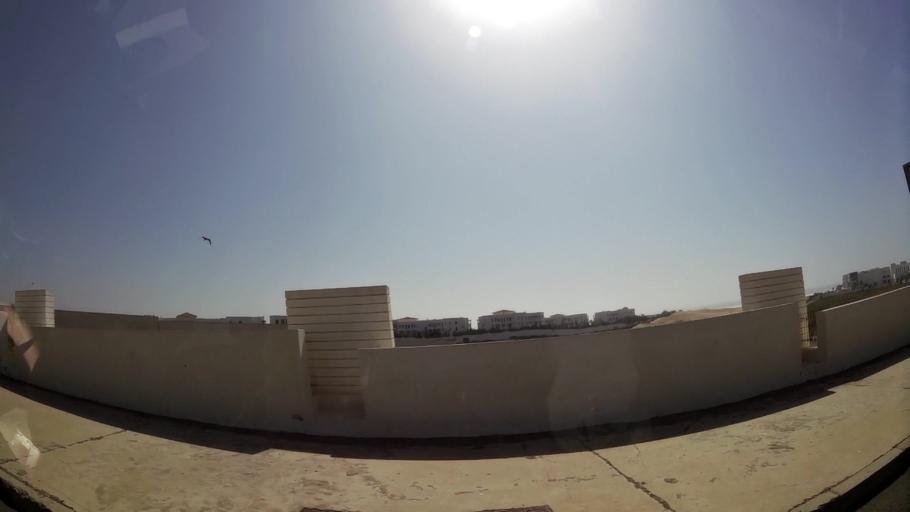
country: MA
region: Souss-Massa-Draa
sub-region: Agadir-Ida-ou-Tnan
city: Agadir
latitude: 30.3900
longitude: -9.5952
